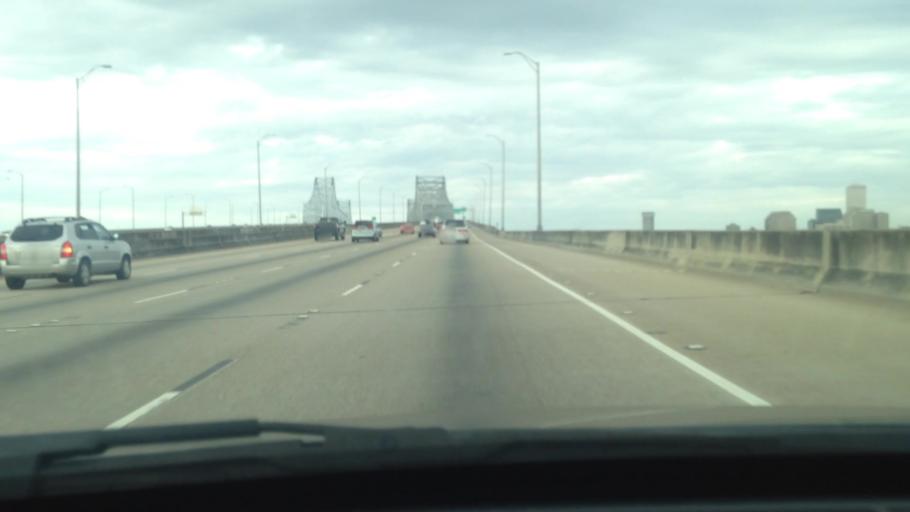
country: US
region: Louisiana
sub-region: Jefferson Parish
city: Gretna
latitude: 29.9385
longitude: -90.0426
